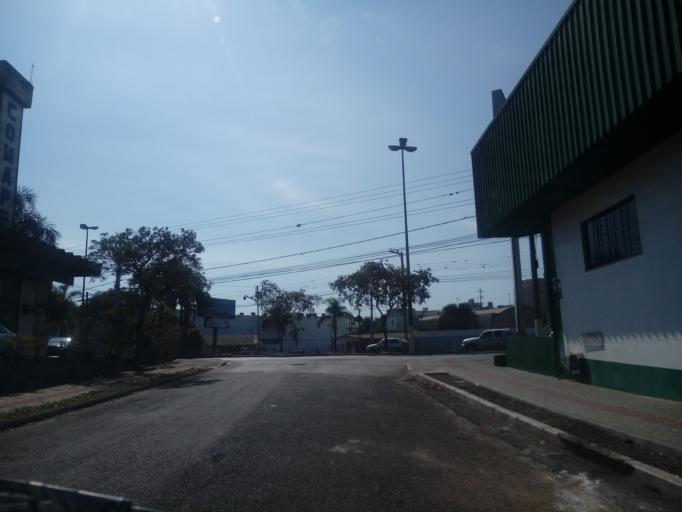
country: BR
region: Santa Catarina
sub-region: Chapeco
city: Chapeco
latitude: -27.0801
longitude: -52.6244
